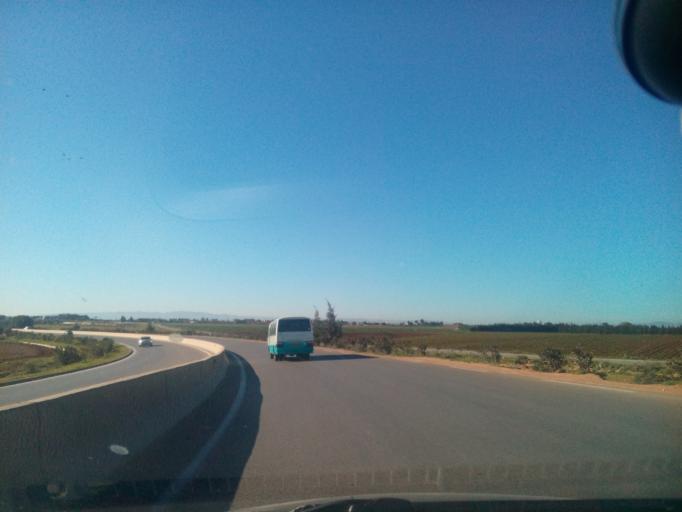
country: DZ
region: Relizane
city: Djidiouia
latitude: 35.8977
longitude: 0.7092
